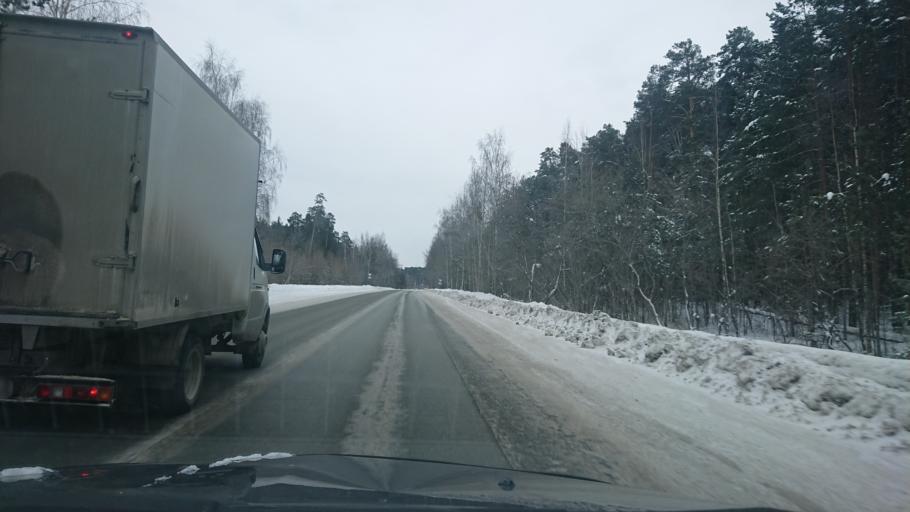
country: RU
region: Sverdlovsk
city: Sovkhoznyy
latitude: 56.8069
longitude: 60.5318
